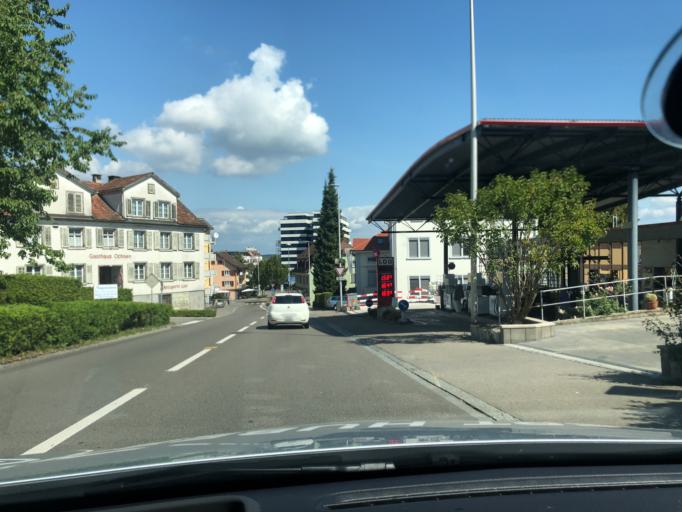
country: CH
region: Thurgau
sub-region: Kreuzlingen District
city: Kreuzlingen
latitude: 47.6433
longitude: 9.1709
